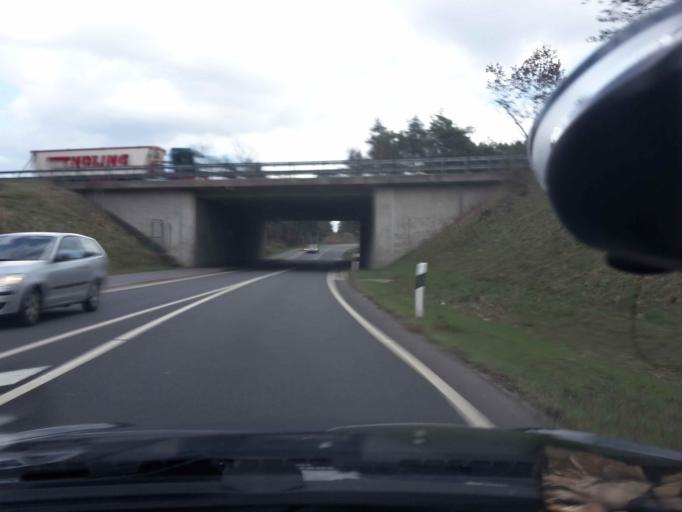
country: DE
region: Lower Saxony
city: Bispingen
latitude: 53.0810
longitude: 9.9629
